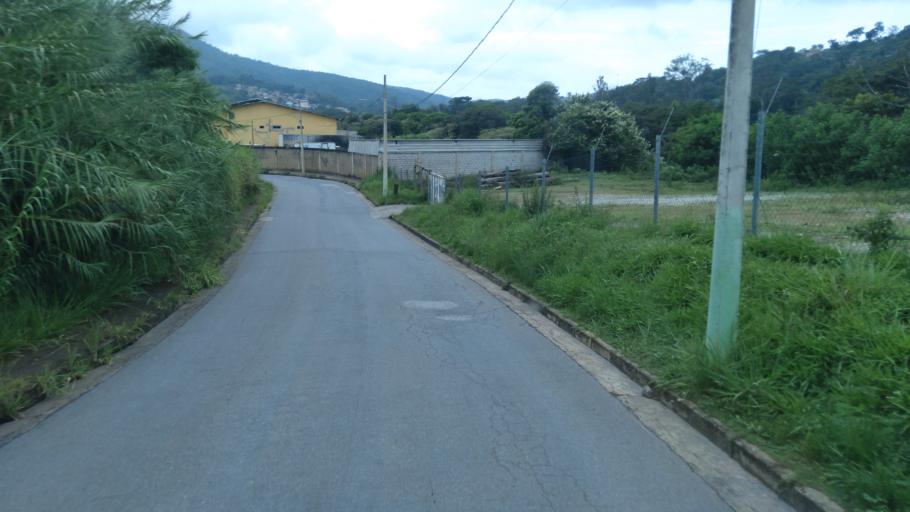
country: BR
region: Minas Gerais
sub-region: Santa Luzia
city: Santa Luzia
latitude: -19.8416
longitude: -43.8742
